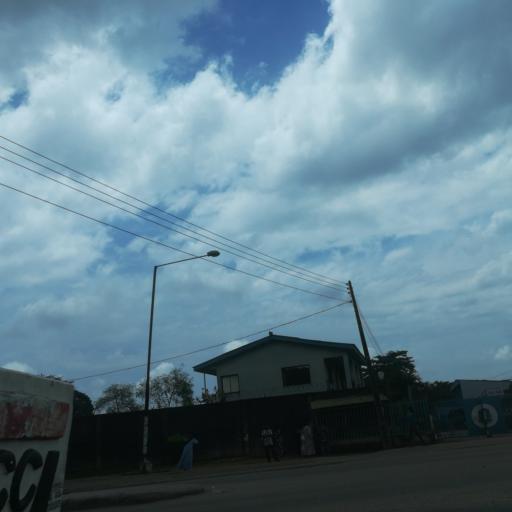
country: NG
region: Lagos
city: Mushin
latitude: 6.5314
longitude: 3.3340
